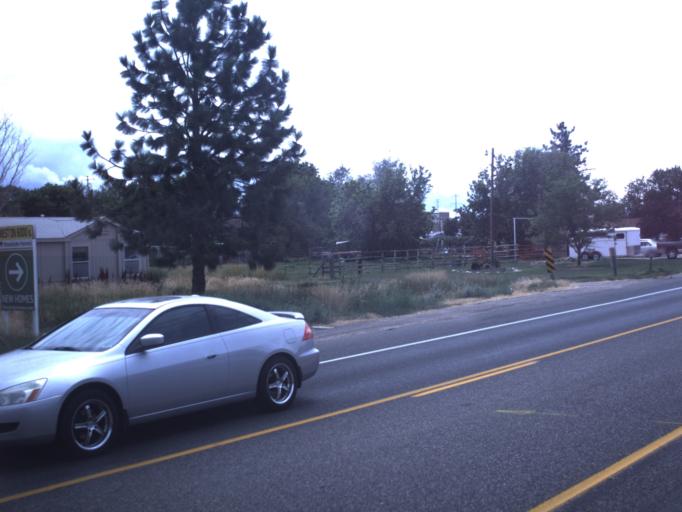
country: US
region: Utah
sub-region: Davis County
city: Clinton
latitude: 41.1557
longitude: -112.0645
